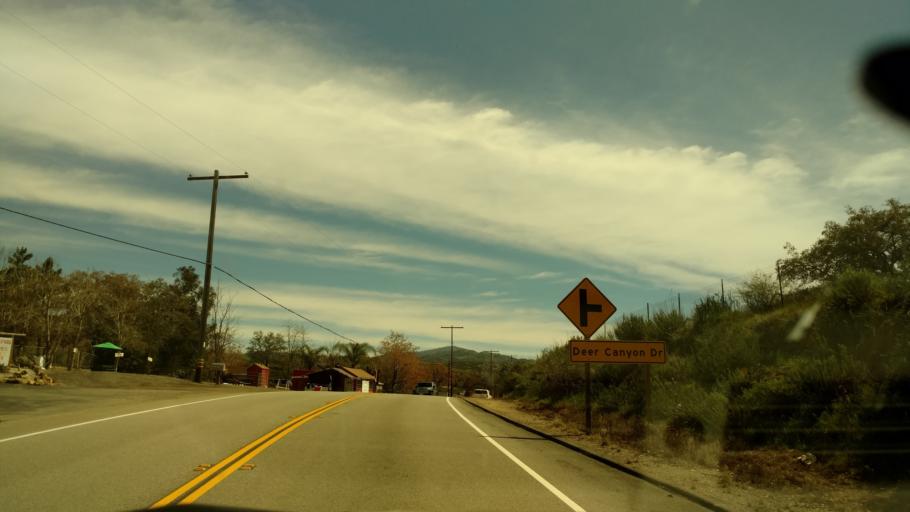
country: US
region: California
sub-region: San Diego County
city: San Diego Country Estates
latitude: 33.0671
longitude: -116.7270
